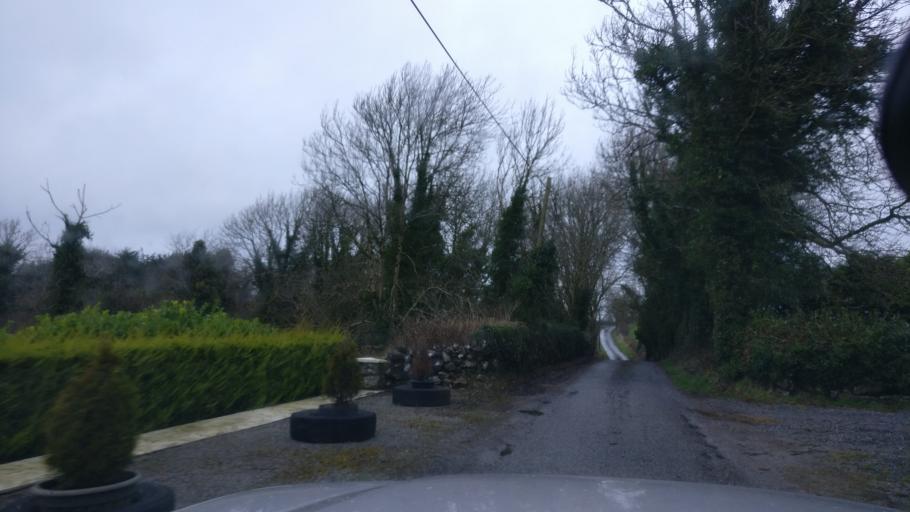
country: IE
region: Connaught
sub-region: County Galway
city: Loughrea
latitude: 53.1672
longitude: -8.6111
